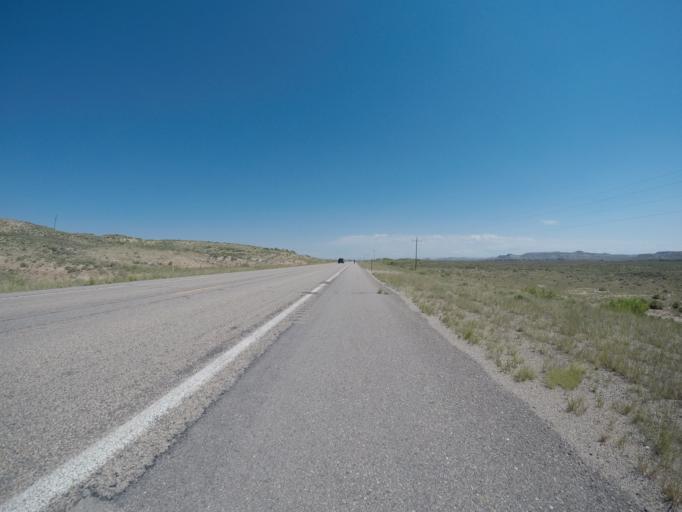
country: US
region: Wyoming
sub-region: Sublette County
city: Marbleton
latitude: 42.3959
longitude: -110.1255
